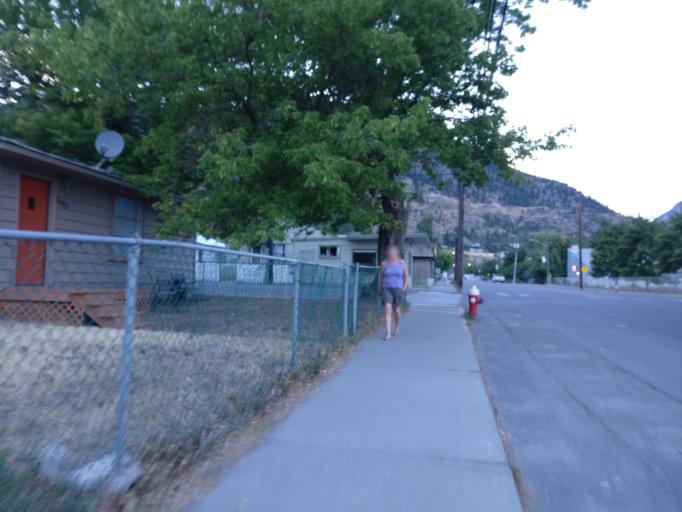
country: CA
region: British Columbia
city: Lillooet
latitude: 50.6885
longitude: -121.9372
